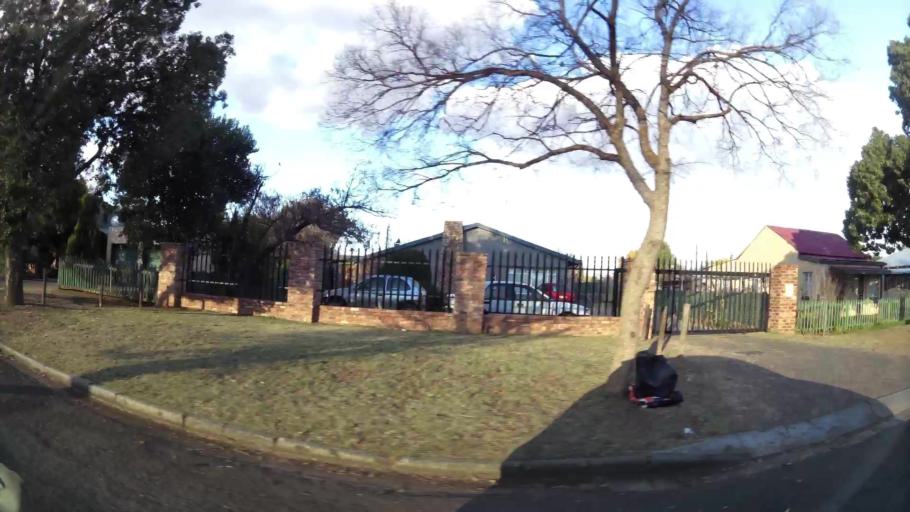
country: ZA
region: North-West
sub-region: Dr Kenneth Kaunda District Municipality
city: Potchefstroom
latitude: -26.7323
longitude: 27.0912
